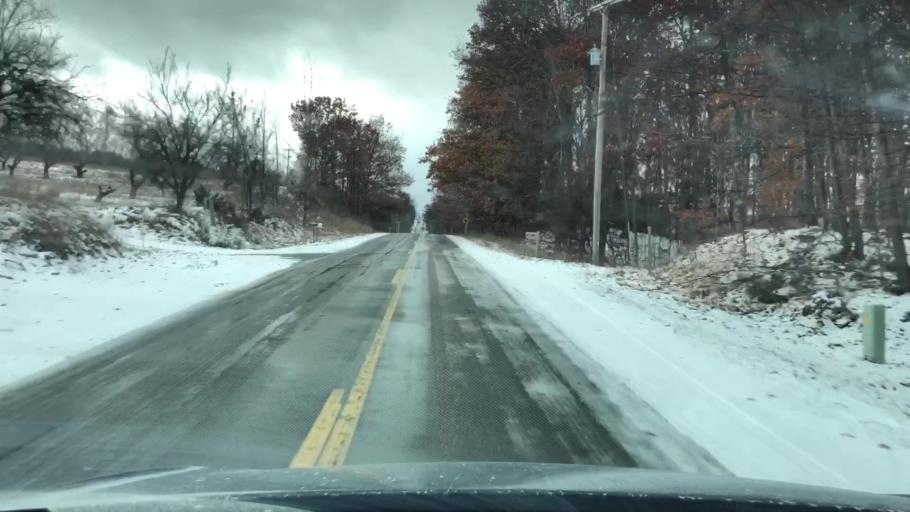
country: US
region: Michigan
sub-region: Antrim County
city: Elk Rapids
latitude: 44.8960
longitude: -85.5154
